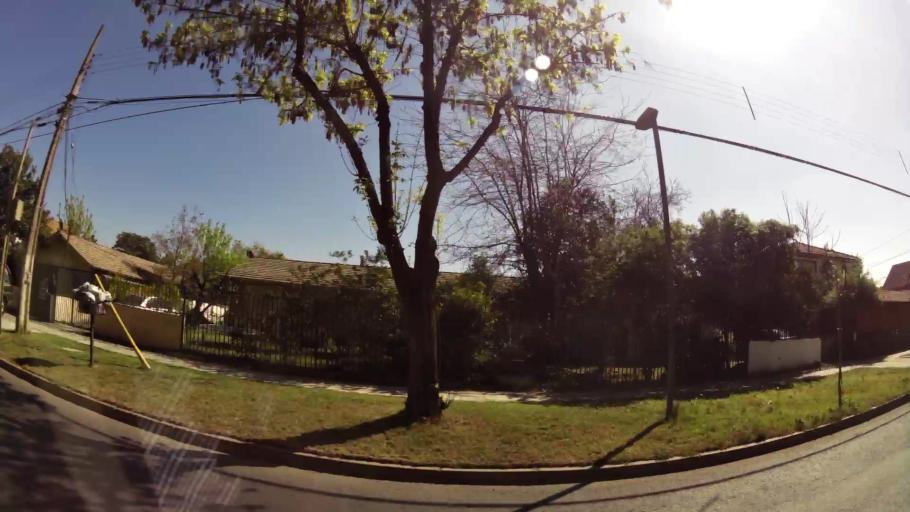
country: CL
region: Santiago Metropolitan
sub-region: Provincia de Santiago
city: Villa Presidente Frei, Nunoa, Santiago, Chile
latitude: -33.4176
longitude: -70.5483
